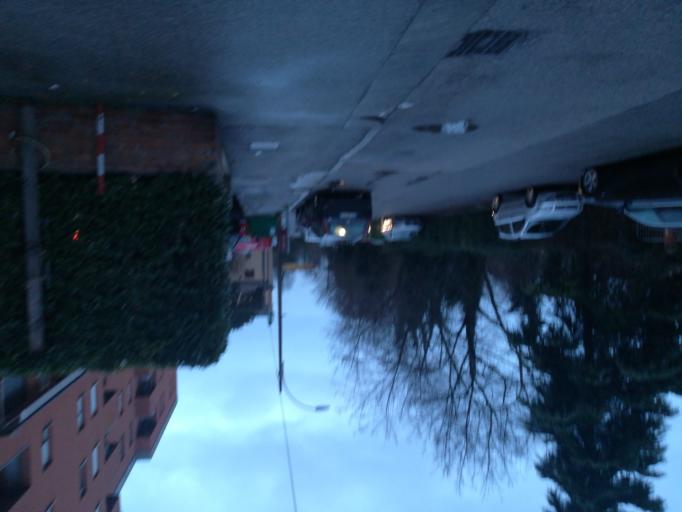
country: IT
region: Emilia-Romagna
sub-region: Provincia di Bologna
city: Progresso
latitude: 44.5494
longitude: 11.3544
